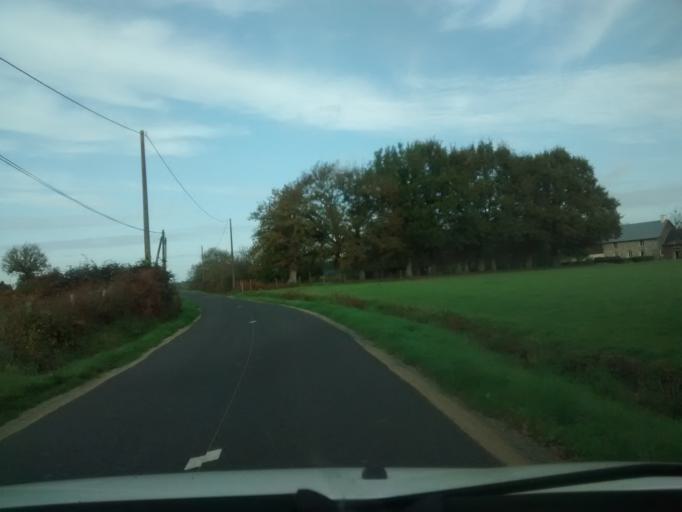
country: FR
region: Brittany
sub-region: Departement d'Ille-et-Vilaine
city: Brece
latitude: 48.1137
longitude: -1.4877
